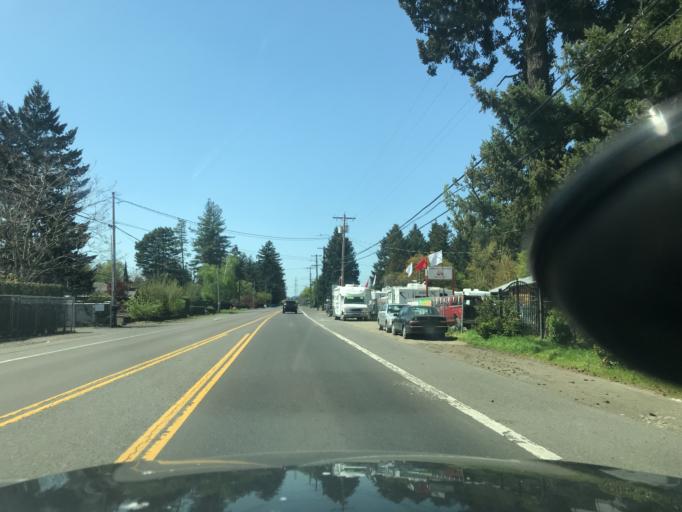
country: US
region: Oregon
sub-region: Multnomah County
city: Lents
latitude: 45.4964
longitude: -122.5498
